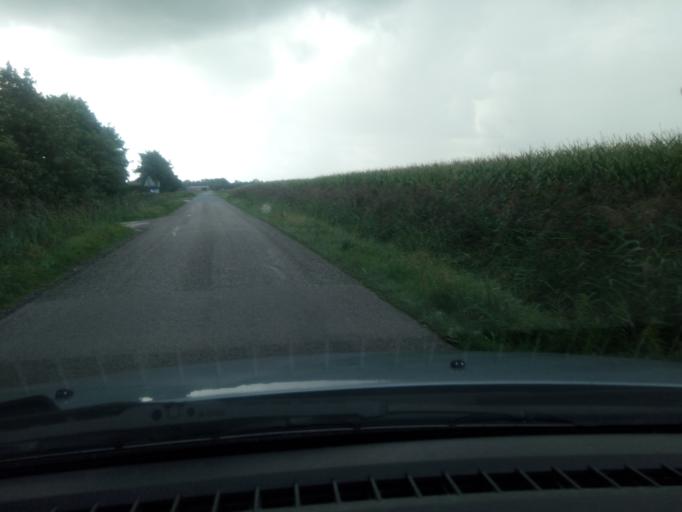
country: NL
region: Groningen
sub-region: Gemeente Grootegast
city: Grootegast
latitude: 53.2534
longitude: 6.2467
